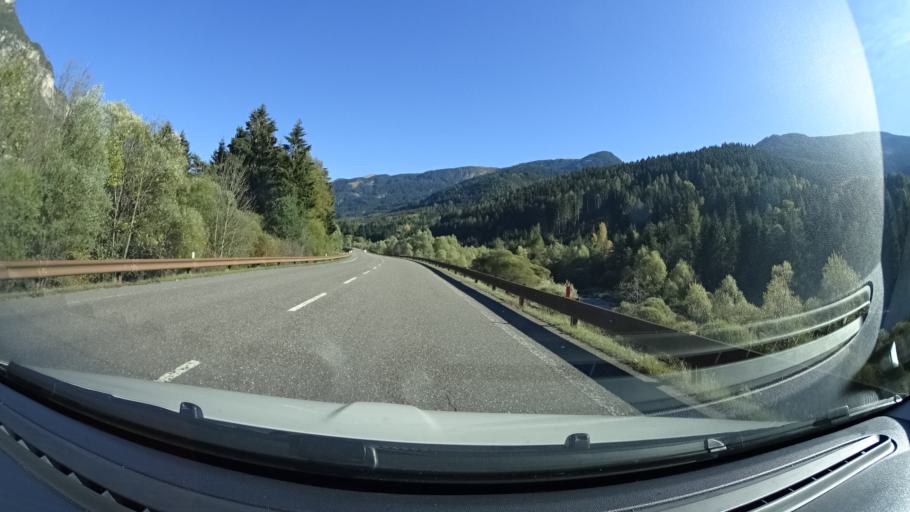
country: IT
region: Trentino-Alto Adige
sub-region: Provincia di Trento
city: Panchia
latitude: 46.2827
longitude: 11.5307
